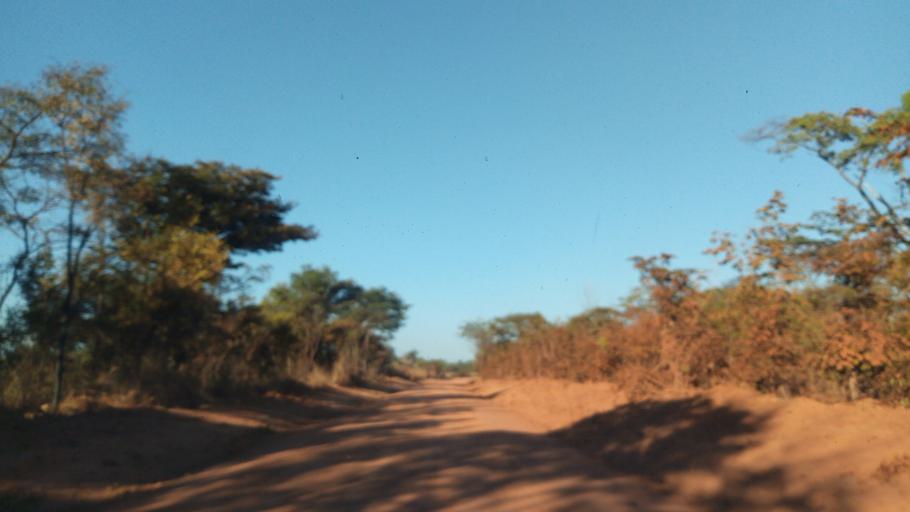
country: ZM
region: Luapula
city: Mwense
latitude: -10.4757
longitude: 28.5132
